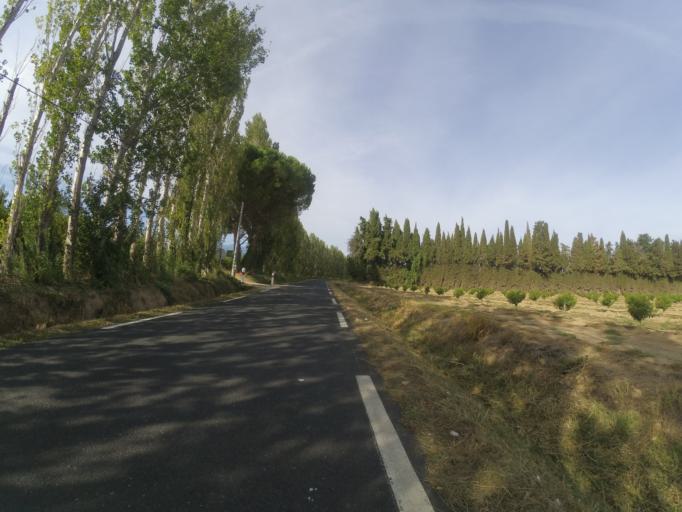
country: FR
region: Languedoc-Roussillon
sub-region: Departement des Pyrenees-Orientales
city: Millas
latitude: 42.6715
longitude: 2.7138
